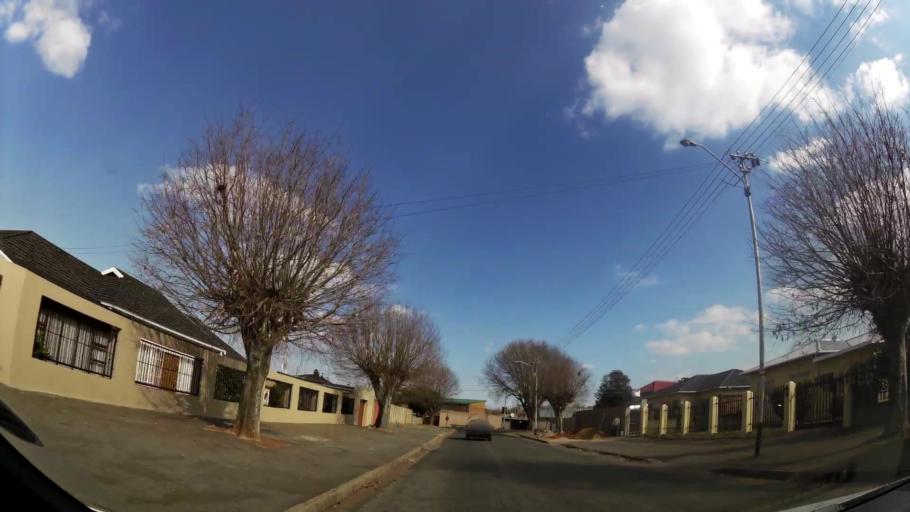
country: ZA
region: Gauteng
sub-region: Ekurhuleni Metropolitan Municipality
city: Germiston
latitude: -26.1790
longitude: 28.1790
